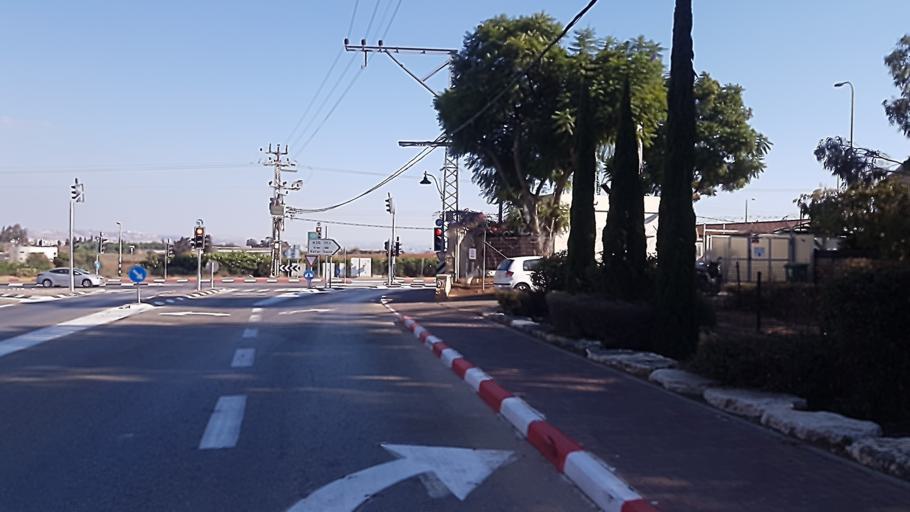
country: IL
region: Central District
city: Kfar Saba
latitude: 32.2003
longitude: 34.9159
